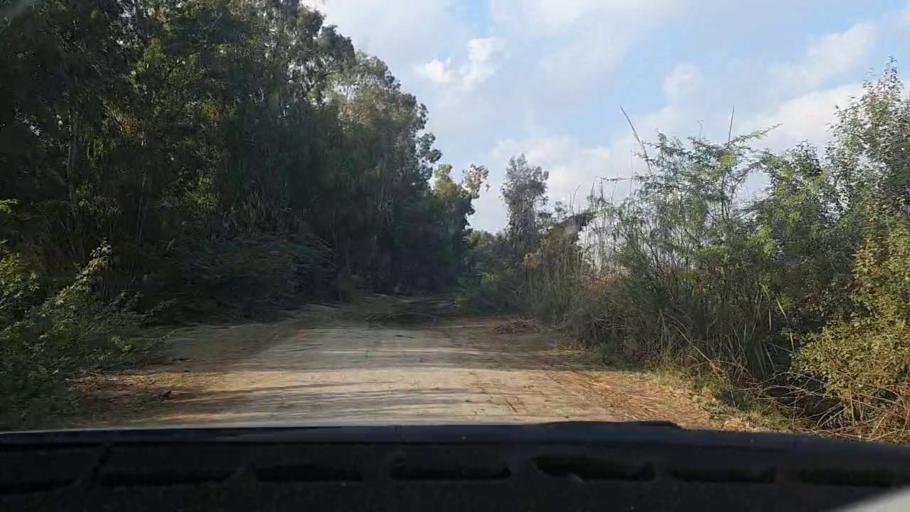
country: PK
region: Sindh
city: Tando Mittha Khan
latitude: 25.9129
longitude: 69.3030
